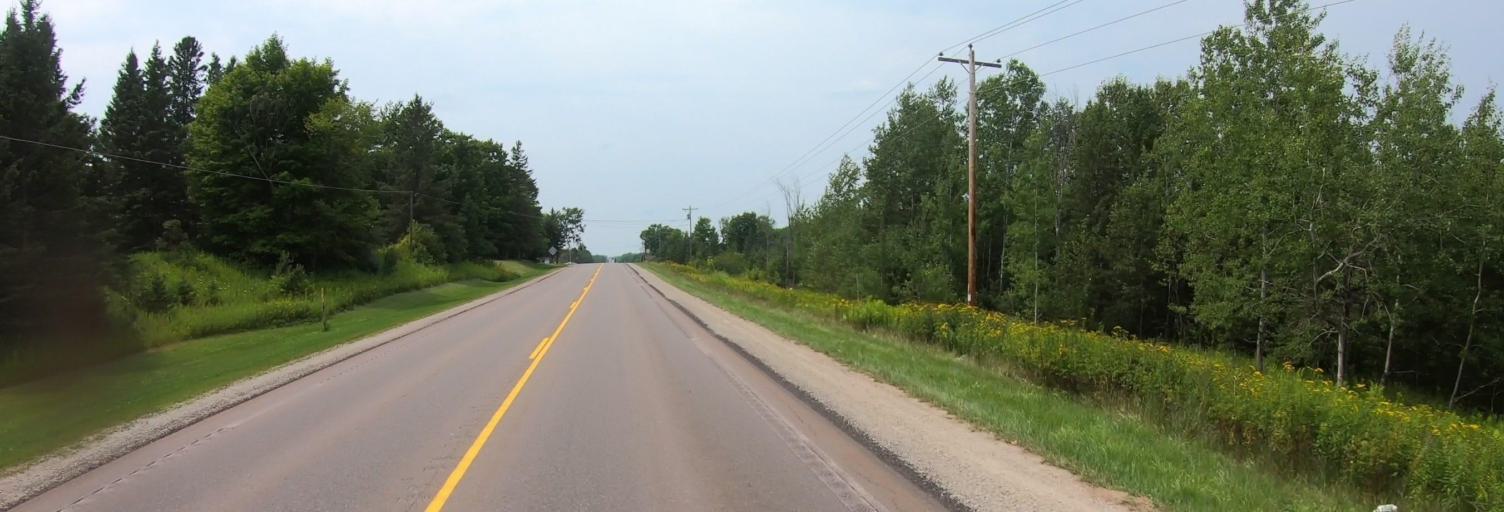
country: US
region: Michigan
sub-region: Alger County
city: Munising
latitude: 46.3476
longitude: -86.9366
